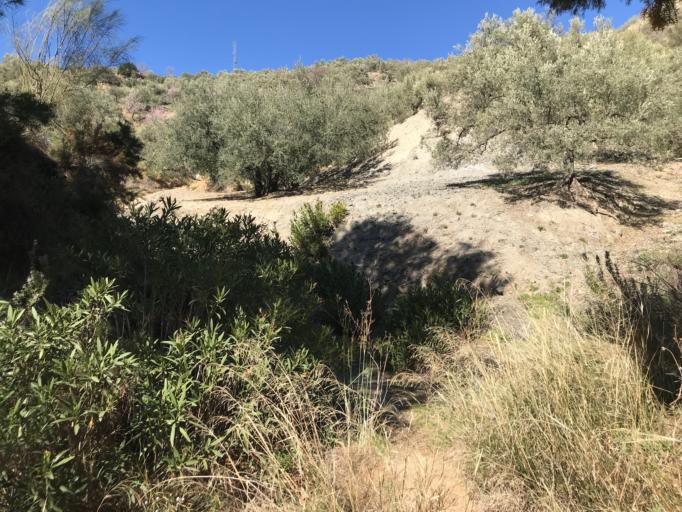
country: ES
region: Andalusia
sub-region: Provincia de Malaga
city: Canillas de Albaida
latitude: 36.8524
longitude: -3.9856
